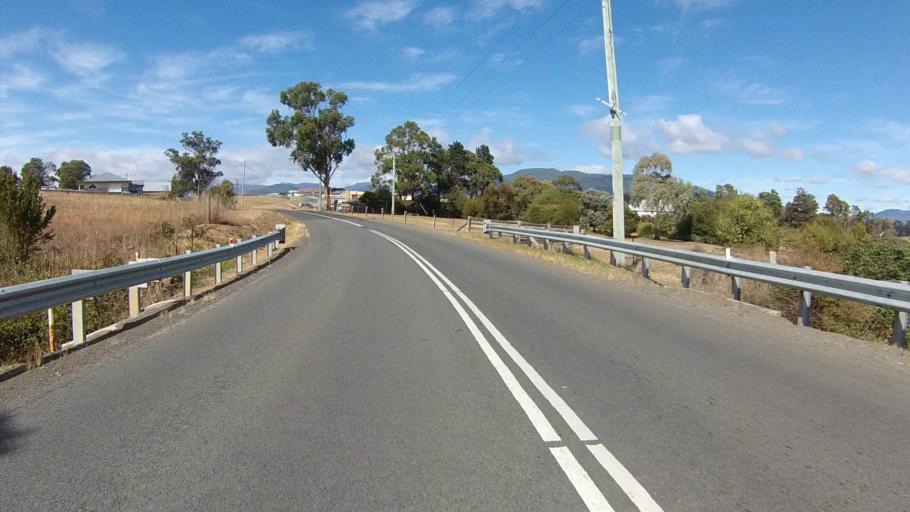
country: AU
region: Tasmania
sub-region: Brighton
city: Old Beach
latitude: -42.7454
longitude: 147.2818
